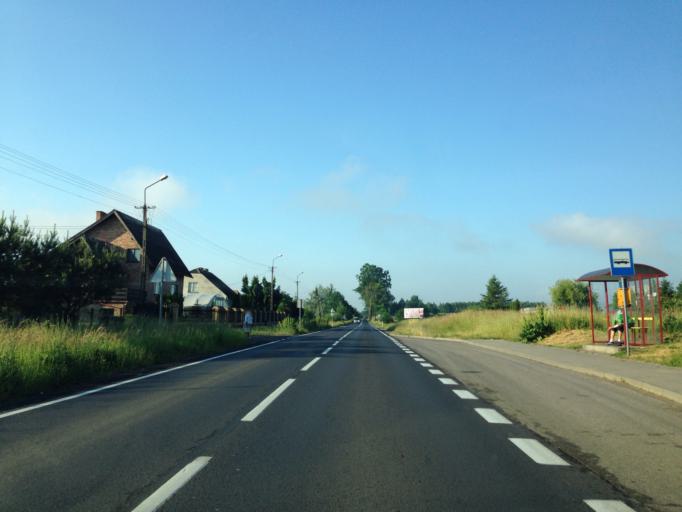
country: PL
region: Kujawsko-Pomorskie
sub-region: Grudziadz
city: Grudziadz
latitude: 53.5215
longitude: 18.8108
